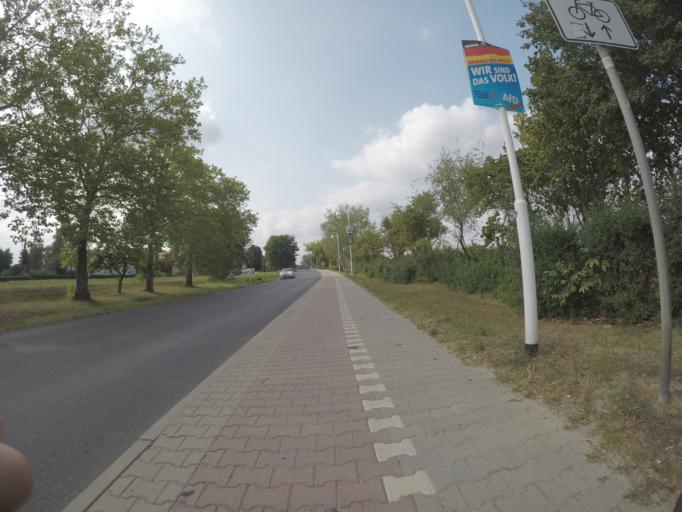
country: DE
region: Berlin
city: Lichtenrade
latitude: 52.3509
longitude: 13.4207
